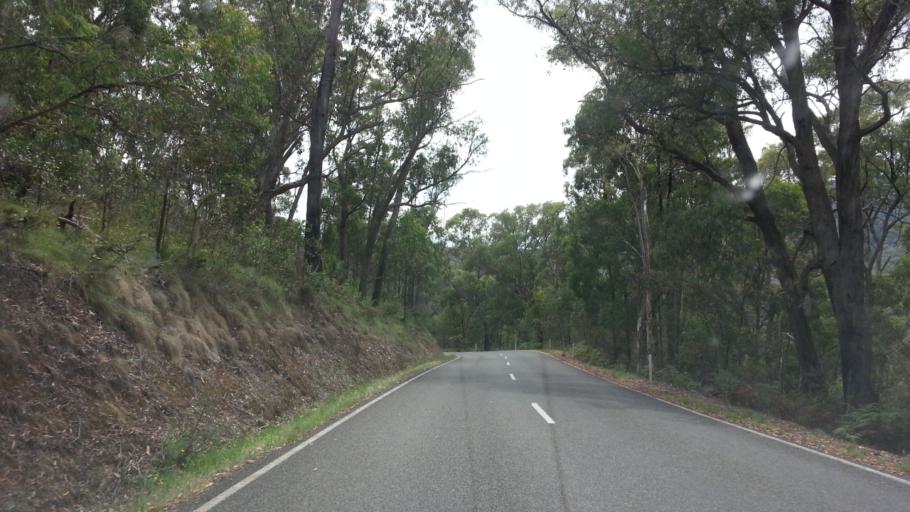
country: AU
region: Victoria
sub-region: Alpine
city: Mount Beauty
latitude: -36.7433
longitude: 147.1903
